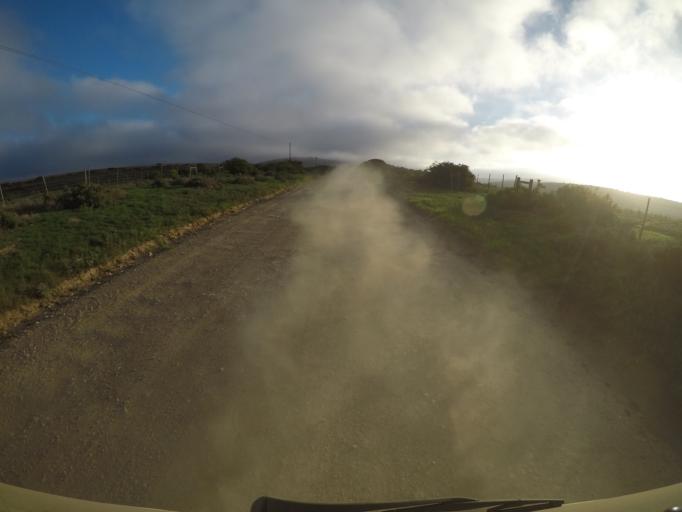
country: ZA
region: Western Cape
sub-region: Eden District Municipality
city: Mossel Bay
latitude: -34.1324
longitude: 22.0450
